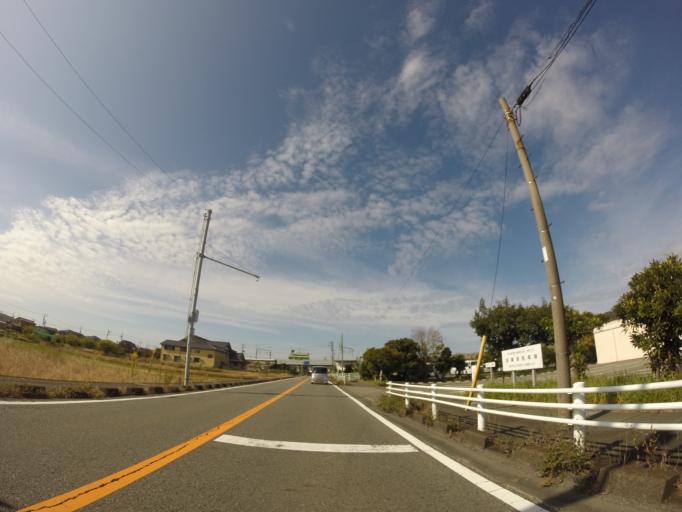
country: JP
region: Shizuoka
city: Yaizu
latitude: 34.8822
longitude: 138.3221
